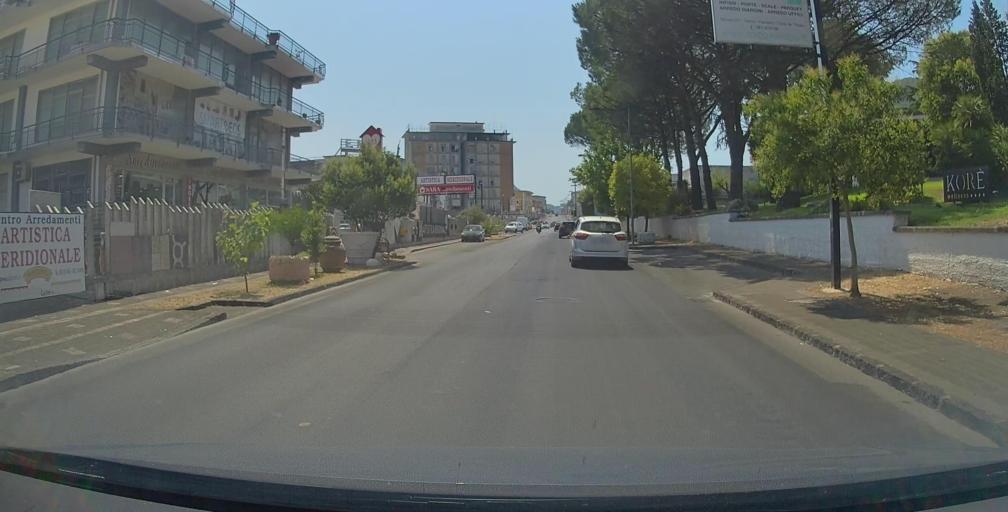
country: IT
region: Campania
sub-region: Provincia di Salerno
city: Nocera Superiore
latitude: 40.7310
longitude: 14.6878
